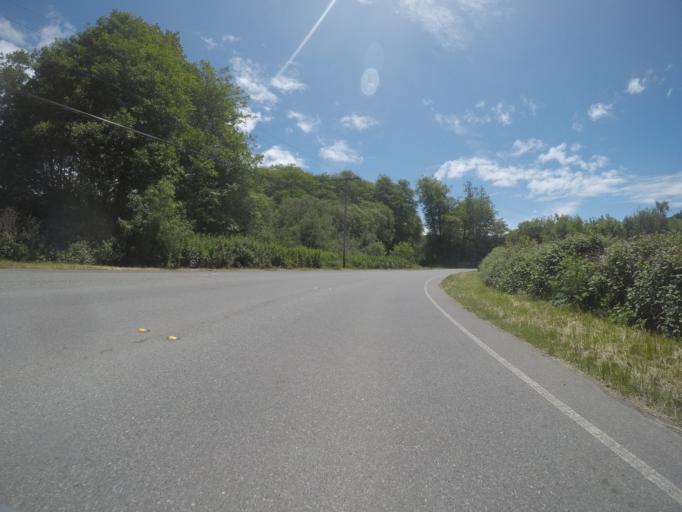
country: US
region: California
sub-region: Del Norte County
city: Bertsch-Oceanview
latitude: 41.5240
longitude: -124.0326
